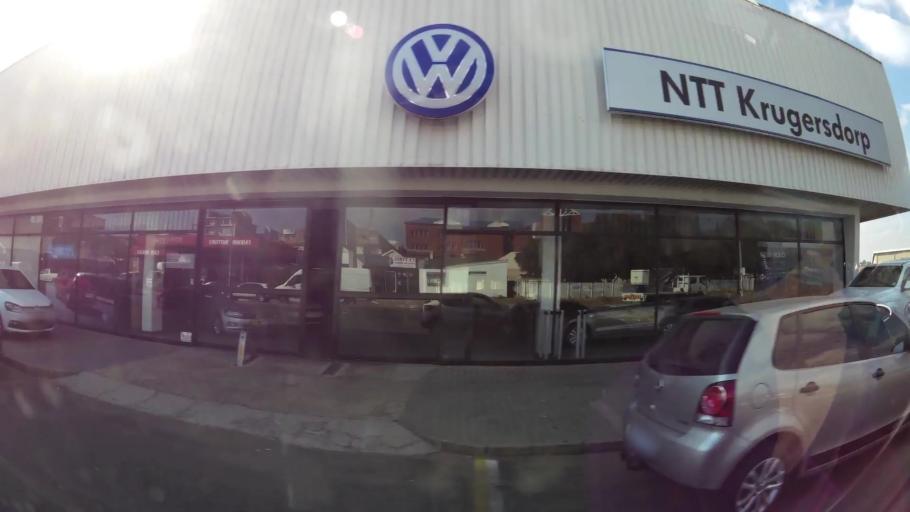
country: ZA
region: Gauteng
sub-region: West Rand District Municipality
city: Krugersdorp
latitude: -26.1029
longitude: 27.7762
